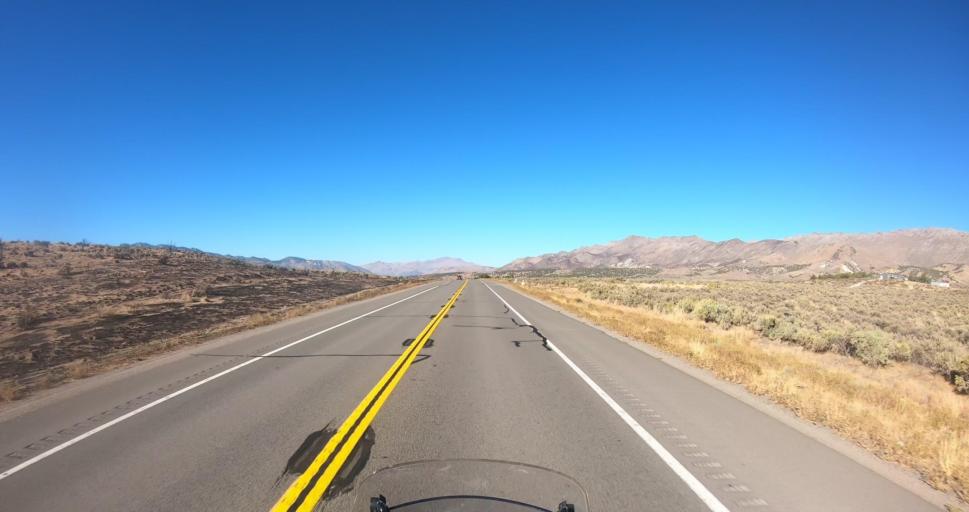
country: US
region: Nevada
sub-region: Washoe County
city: Cold Springs
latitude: 39.8031
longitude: -120.0359
